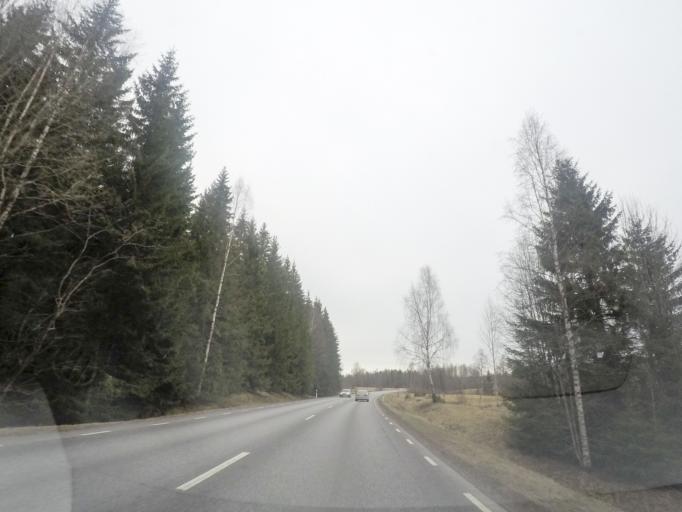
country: SE
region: Vaestmanland
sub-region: Skinnskattebergs Kommun
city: Skinnskatteberg
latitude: 59.8645
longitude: 15.6522
